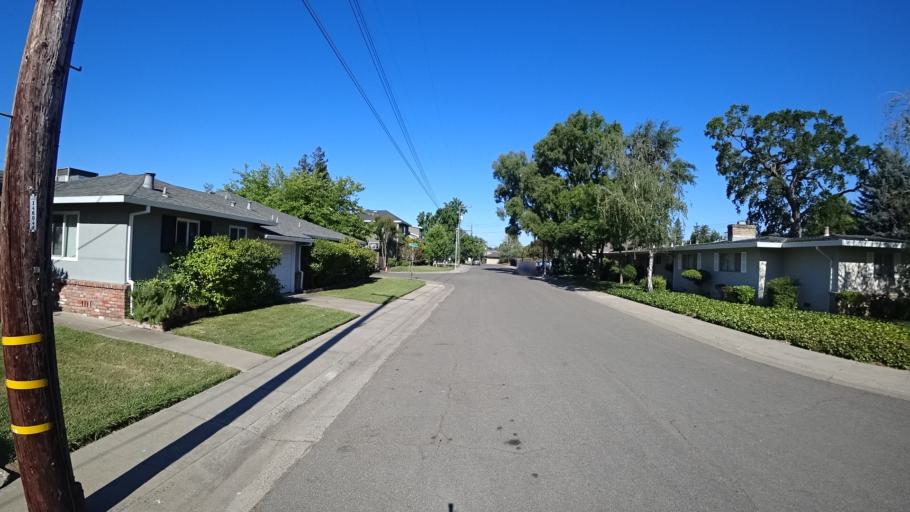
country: US
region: California
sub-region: Sacramento County
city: Parkway
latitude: 38.5255
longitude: -121.5067
